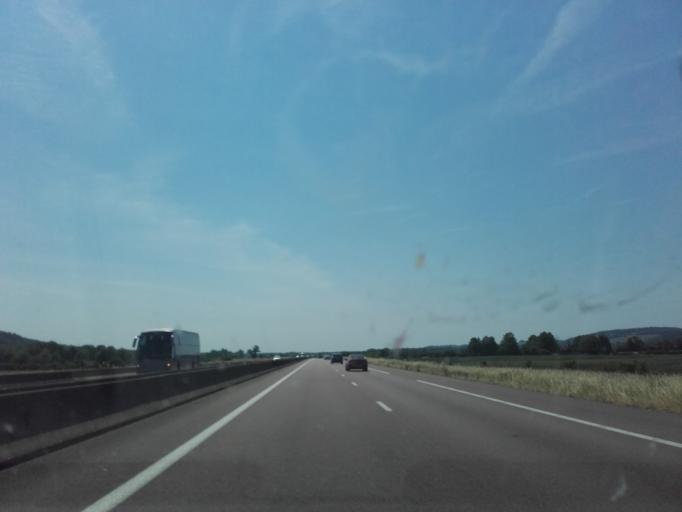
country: FR
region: Bourgogne
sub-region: Departement de la Cote-d'Or
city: Pouilly-en-Auxois
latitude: 47.2978
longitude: 4.5044
